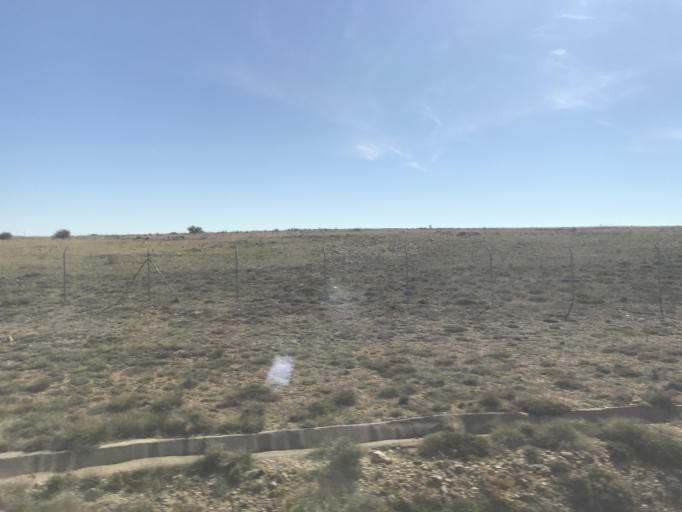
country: ES
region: Castille-La Mancha
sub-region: Provincia de Guadalajara
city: Anguita
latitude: 41.1135
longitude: -2.3589
